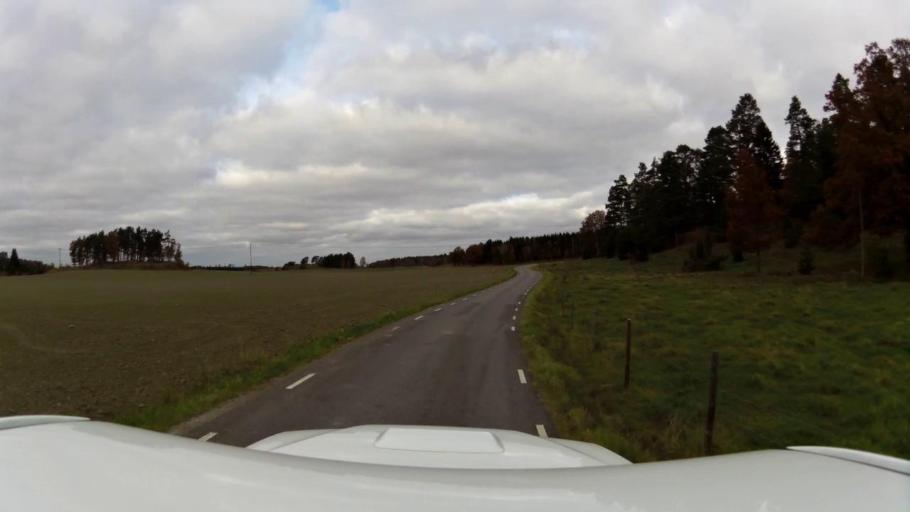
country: SE
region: OEstergoetland
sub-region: Linkopings Kommun
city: Linghem
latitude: 58.3789
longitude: 15.8209
